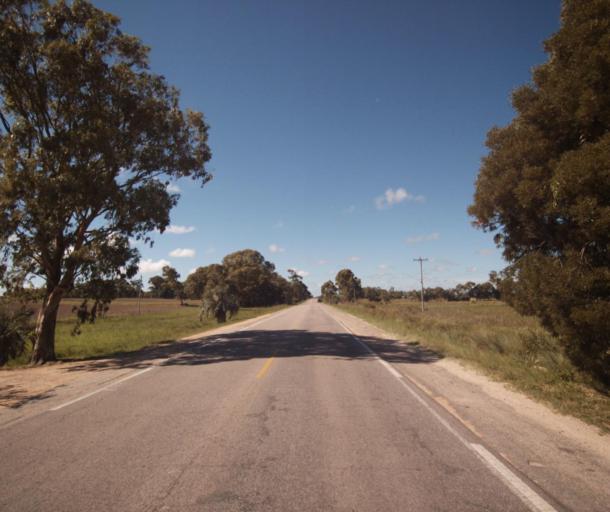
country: BR
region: Rio Grande do Sul
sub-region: Chui
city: Chui
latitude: -33.6637
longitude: -53.4374
